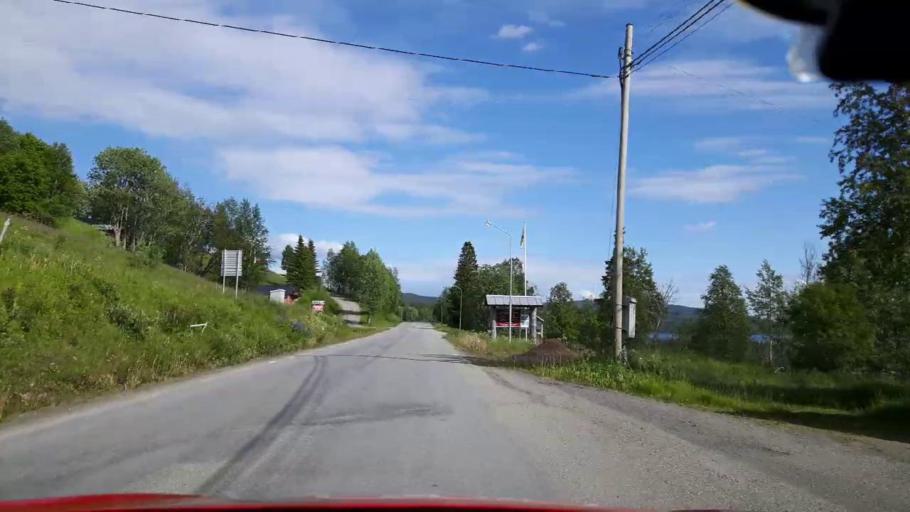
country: SE
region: Jaemtland
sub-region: Krokoms Kommun
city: Valla
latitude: 63.7675
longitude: 14.0676
